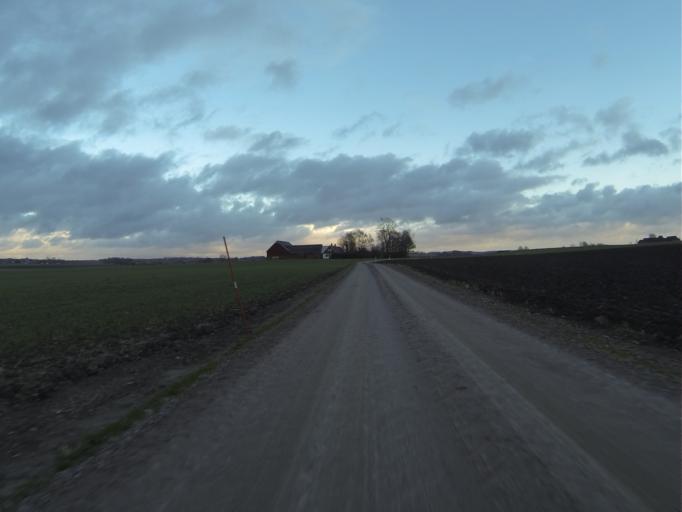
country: SE
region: Skane
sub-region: Lunds Kommun
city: Genarp
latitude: 55.6458
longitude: 13.3158
